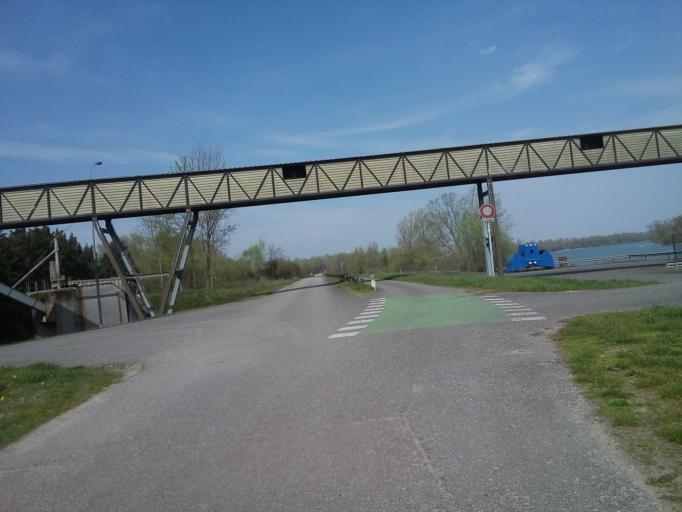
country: FR
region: Alsace
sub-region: Departement du Bas-Rhin
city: Seltz
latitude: 48.8617
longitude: 8.1085
